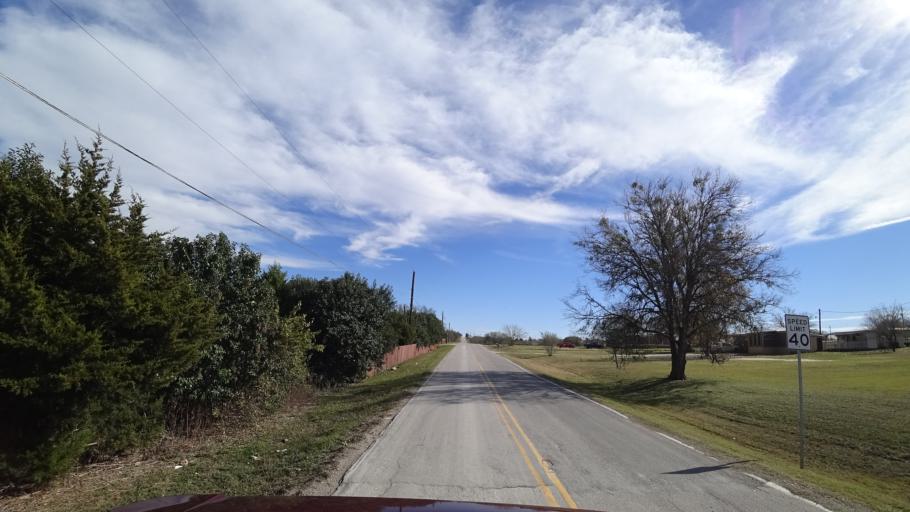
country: US
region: Texas
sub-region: Travis County
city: Onion Creek
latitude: 30.1239
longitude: -97.7402
